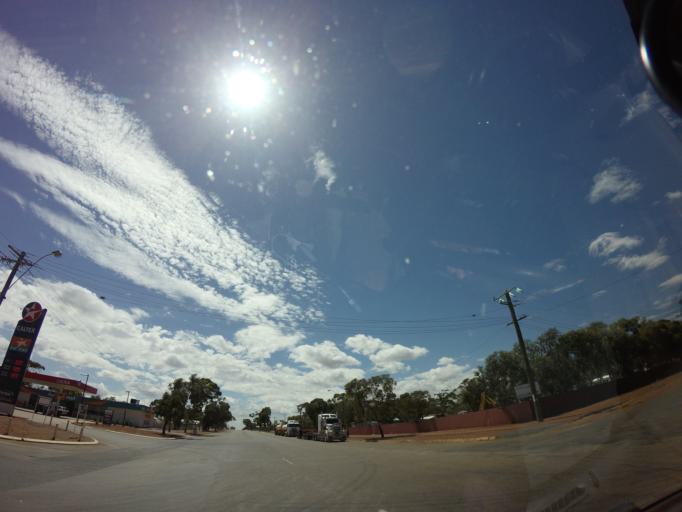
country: AU
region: Western Australia
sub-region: Kalgoorlie/Boulder
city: Boulder
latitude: -30.9546
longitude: 121.1584
